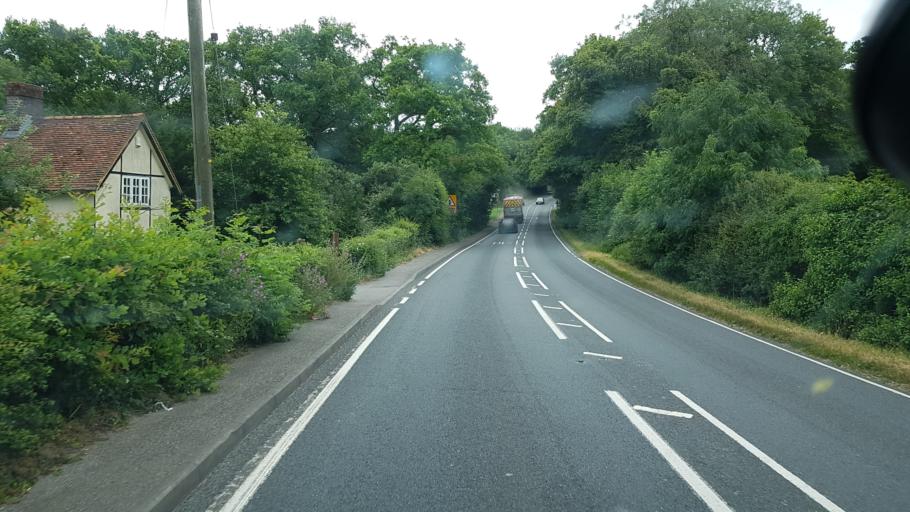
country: GB
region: England
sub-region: Surrey
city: Godstone
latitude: 51.2288
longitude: -0.0476
